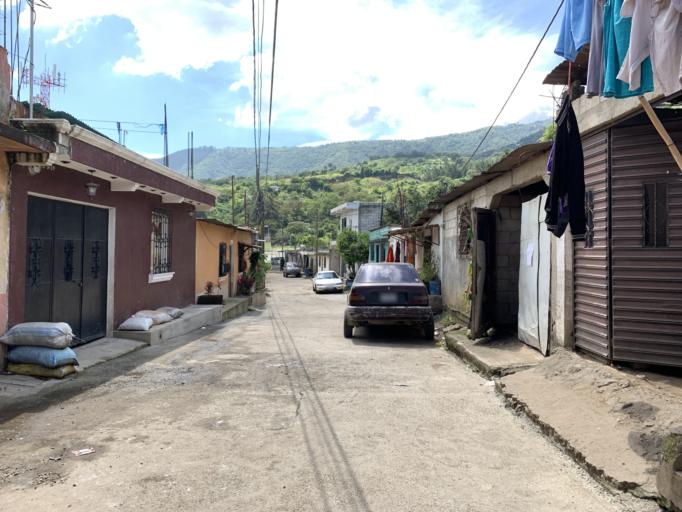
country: GT
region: Guatemala
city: Amatitlan
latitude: 14.4899
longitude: -90.6436
